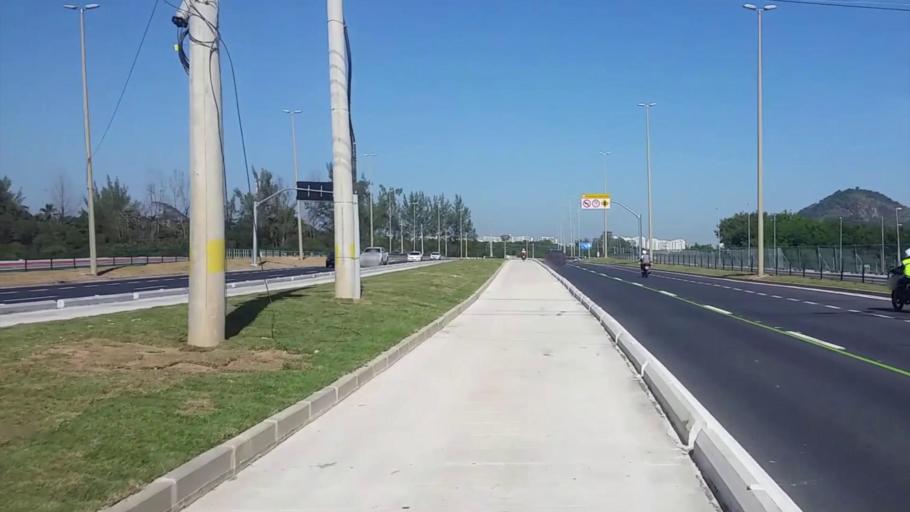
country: BR
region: Rio de Janeiro
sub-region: Nilopolis
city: Nilopolis
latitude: -22.9782
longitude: -43.4075
